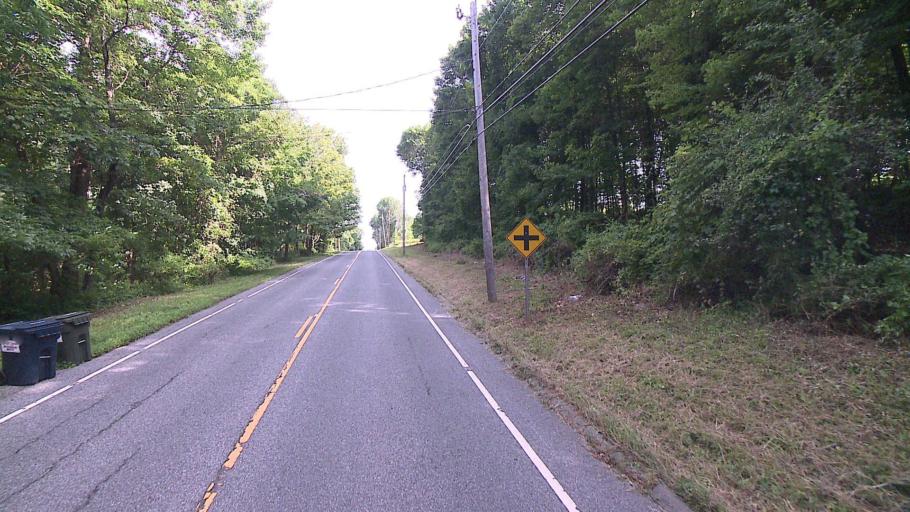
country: US
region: Connecticut
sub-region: Fairfield County
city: Sherman
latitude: 41.5550
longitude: -73.5040
